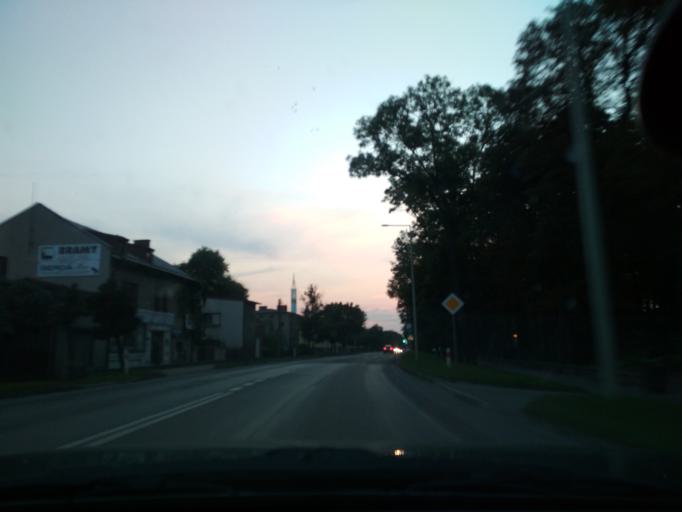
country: PL
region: Silesian Voivodeship
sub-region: Powiat zawiercianski
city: Zawiercie
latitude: 50.4788
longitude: 19.4464
